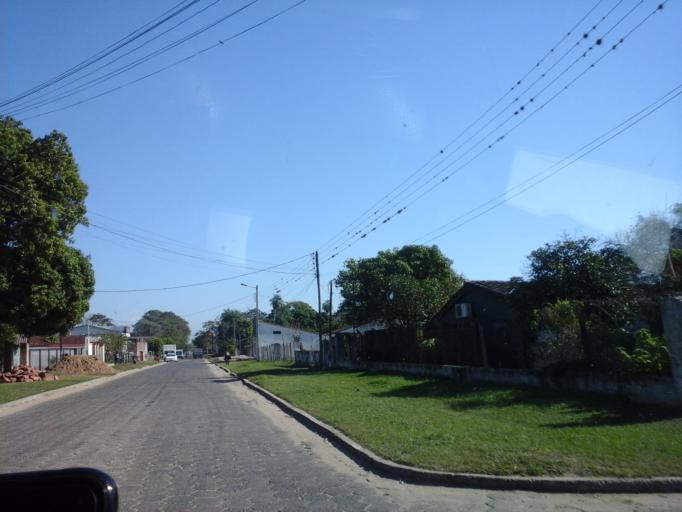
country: PY
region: Neembucu
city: Pilar
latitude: -26.8639
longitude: -58.3046
